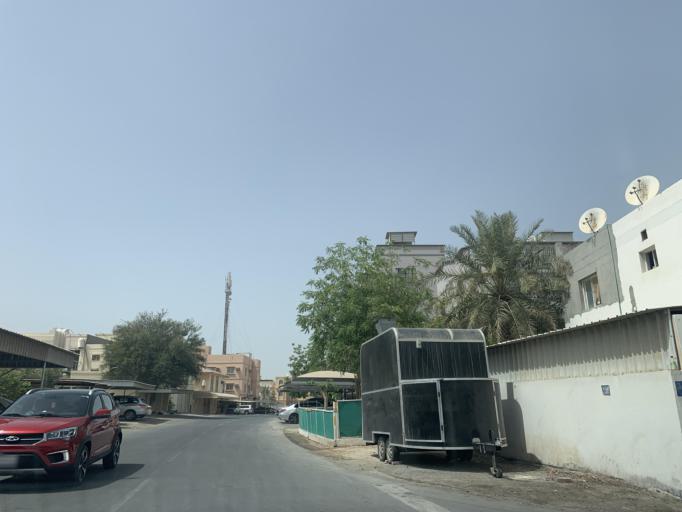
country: BH
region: Northern
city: Madinat `Isa
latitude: 26.1558
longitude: 50.5225
